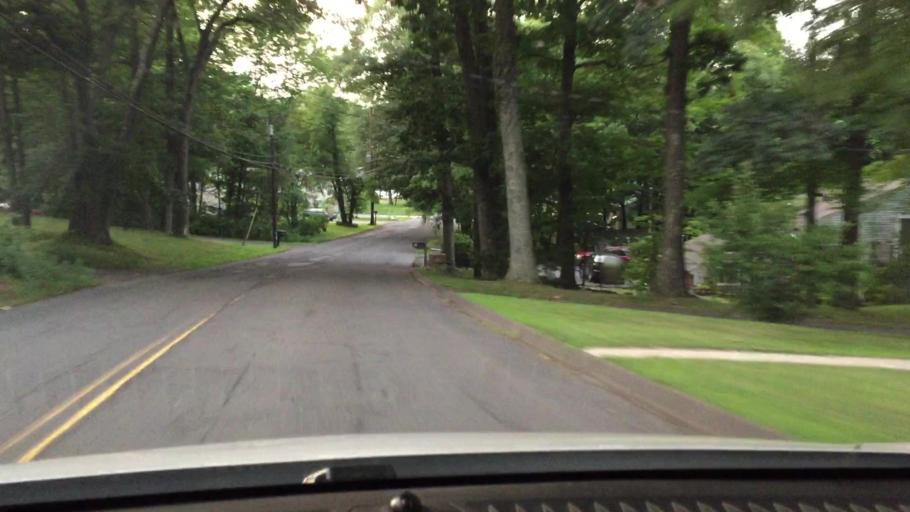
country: US
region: Massachusetts
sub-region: Hampden County
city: Westfield
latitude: 42.1442
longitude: -72.8136
